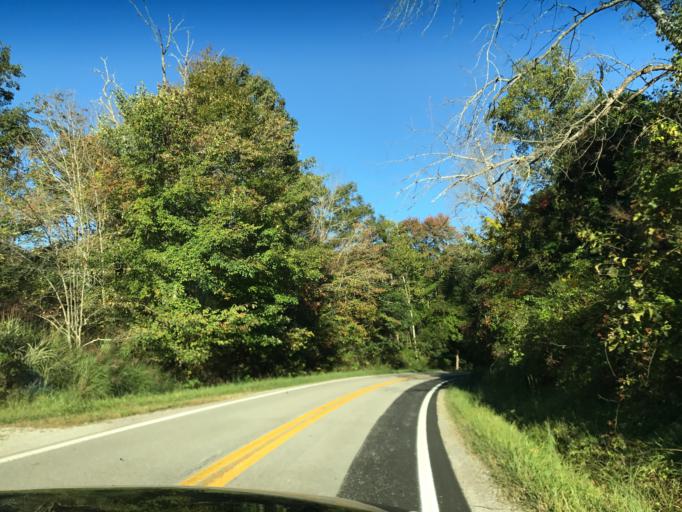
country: US
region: West Virginia
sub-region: Ritchie County
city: Harrisville
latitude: 39.2821
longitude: -81.0878
